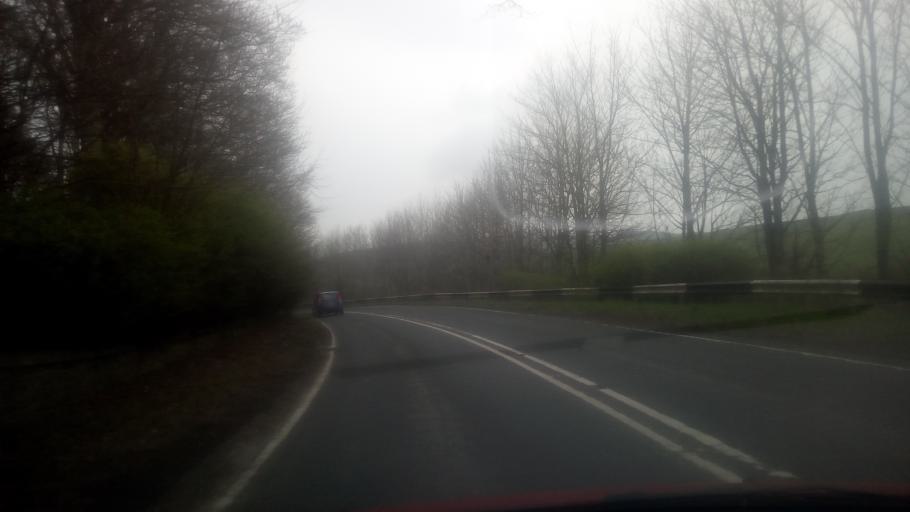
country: GB
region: Scotland
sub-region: The Scottish Borders
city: Galashiels
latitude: 55.6846
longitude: -2.8683
